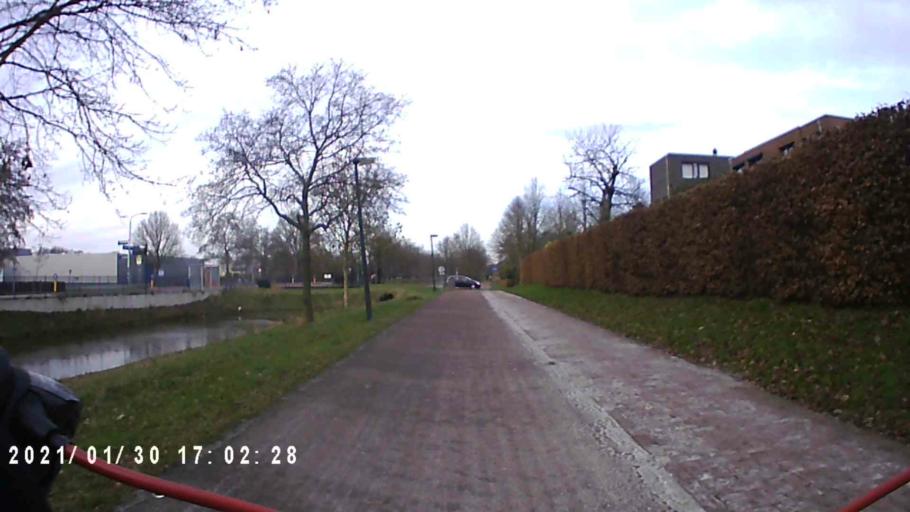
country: NL
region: Groningen
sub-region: Gemeente Leek
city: Leek
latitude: 53.1538
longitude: 6.3708
